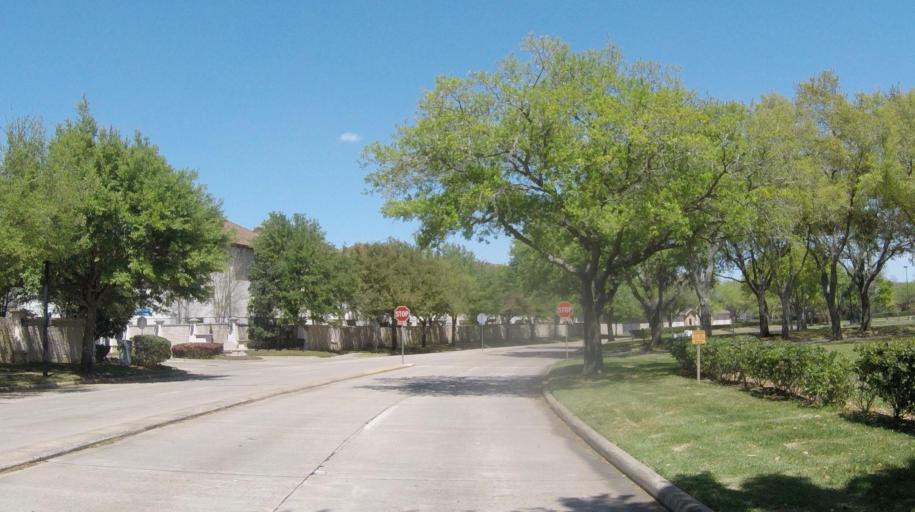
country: US
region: Texas
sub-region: Fort Bend County
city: Sugar Land
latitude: 29.6078
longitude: -95.6285
